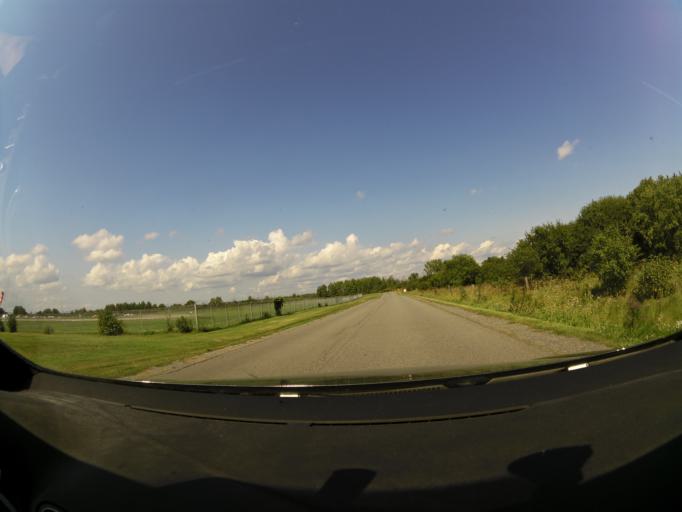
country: CA
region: Quebec
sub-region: Outaouais
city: Gatineau
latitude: 45.4605
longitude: -75.6359
